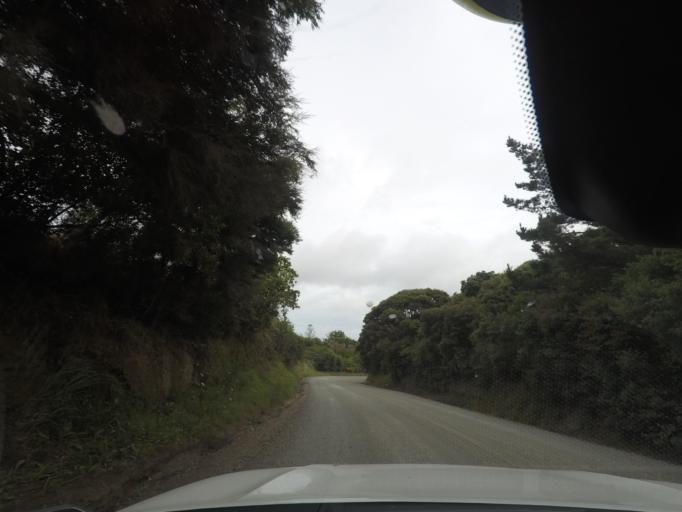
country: NZ
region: Auckland
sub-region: Auckland
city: Parakai
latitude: -36.4843
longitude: 174.2517
